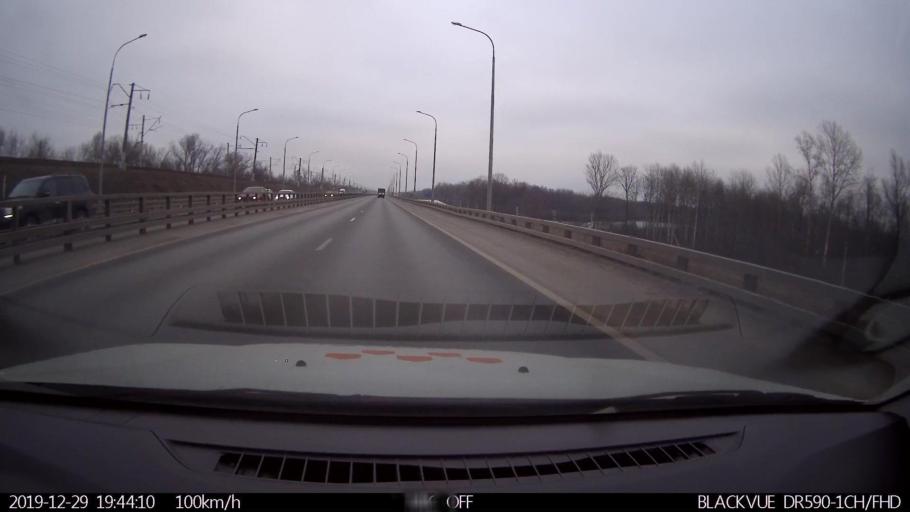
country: RU
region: Nizjnij Novgorod
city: Neklyudovo
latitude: 56.3715
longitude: 43.9459
